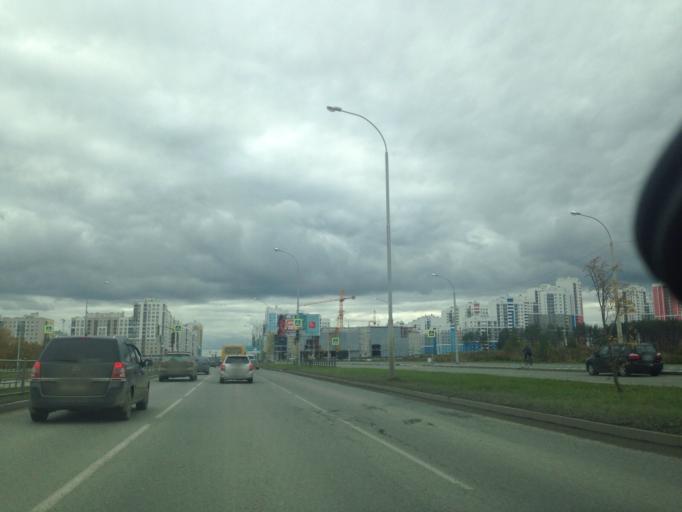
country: RU
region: Sverdlovsk
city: Sovkhoznyy
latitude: 56.7962
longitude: 60.5271
